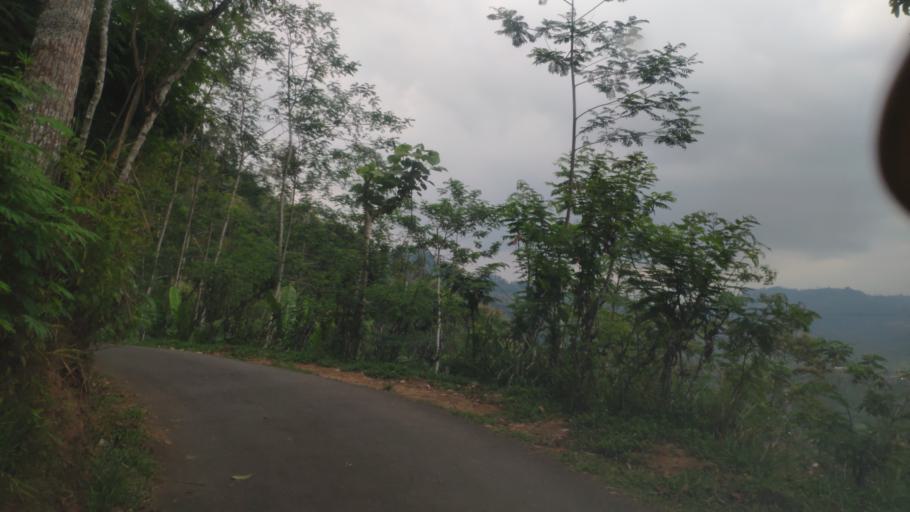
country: ID
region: Central Java
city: Wonosobo
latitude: -7.2736
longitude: 109.7659
